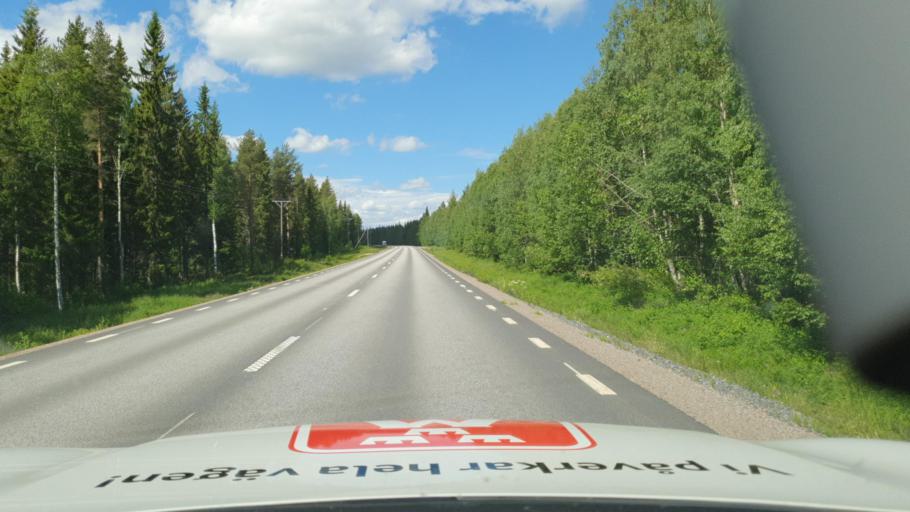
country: SE
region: Vaesterbotten
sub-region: Skelleftea Kommun
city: Boliden
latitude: 64.9240
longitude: 20.3237
